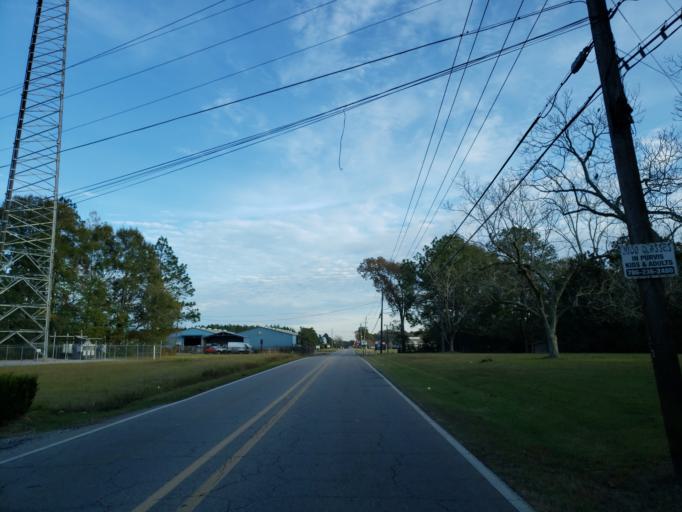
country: US
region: Mississippi
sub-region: Lamar County
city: Purvis
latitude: 31.1558
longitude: -89.4180
